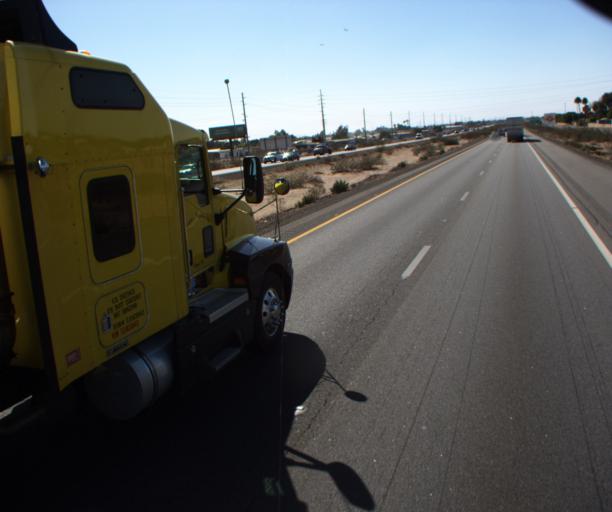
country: US
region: Arizona
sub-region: Yuma County
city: Fortuna Foothills
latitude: 32.6707
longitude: -114.4670
